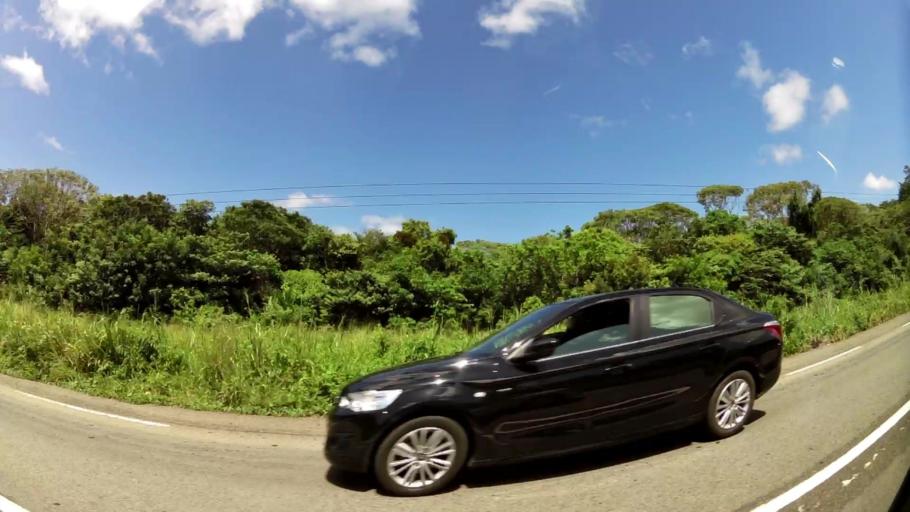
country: GF
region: Guyane
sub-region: Guyane
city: Matoury
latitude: 4.8660
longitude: -52.3342
